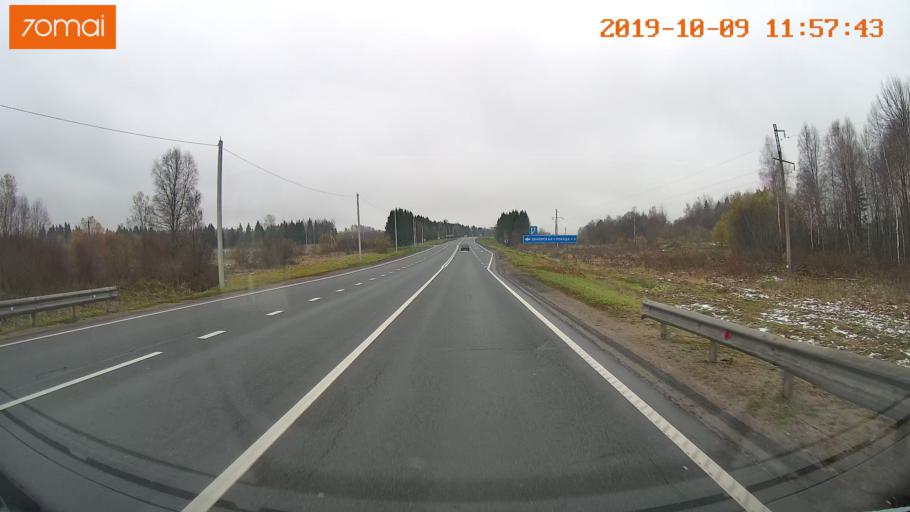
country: RU
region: Vologda
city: Gryazovets
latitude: 58.7285
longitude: 40.2942
